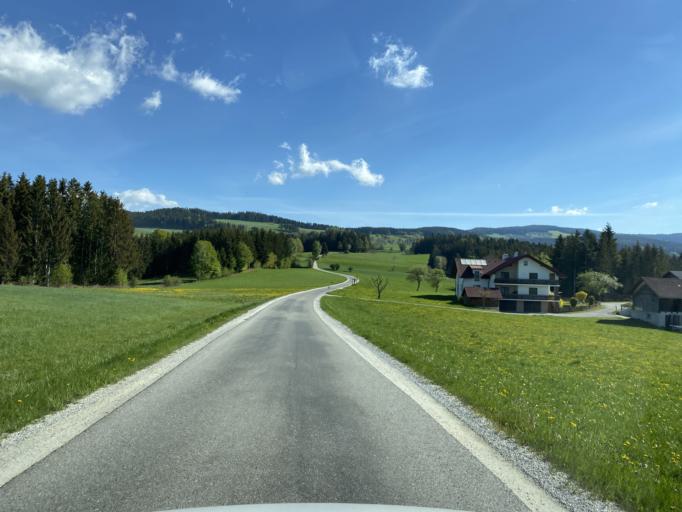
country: AT
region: Styria
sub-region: Politischer Bezirk Weiz
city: Strallegg
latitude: 47.3709
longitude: 15.7162
